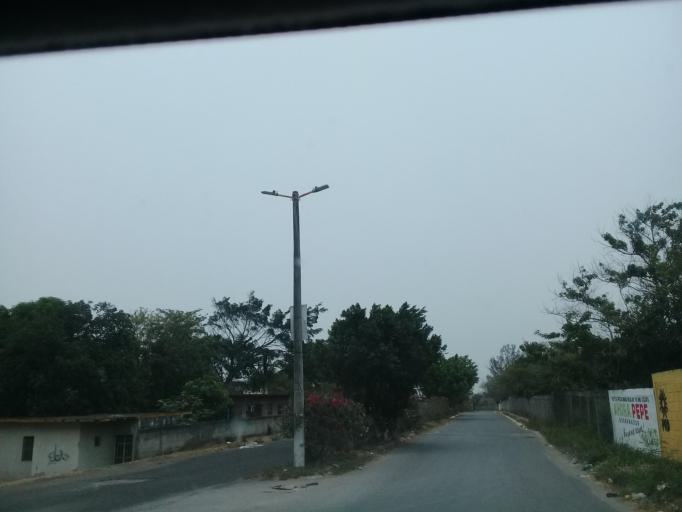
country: MX
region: Veracruz
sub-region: Veracruz
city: Las Amapolas
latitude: 19.1553
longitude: -96.2120
